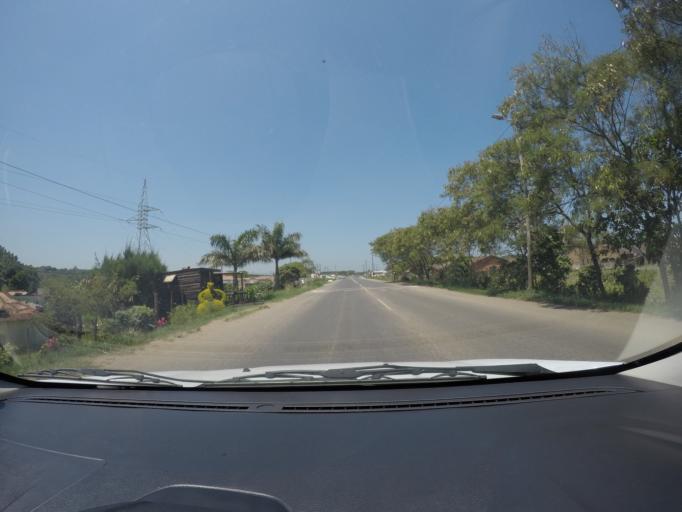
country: ZA
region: KwaZulu-Natal
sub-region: uThungulu District Municipality
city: eSikhawini
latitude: -28.8588
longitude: 31.9216
